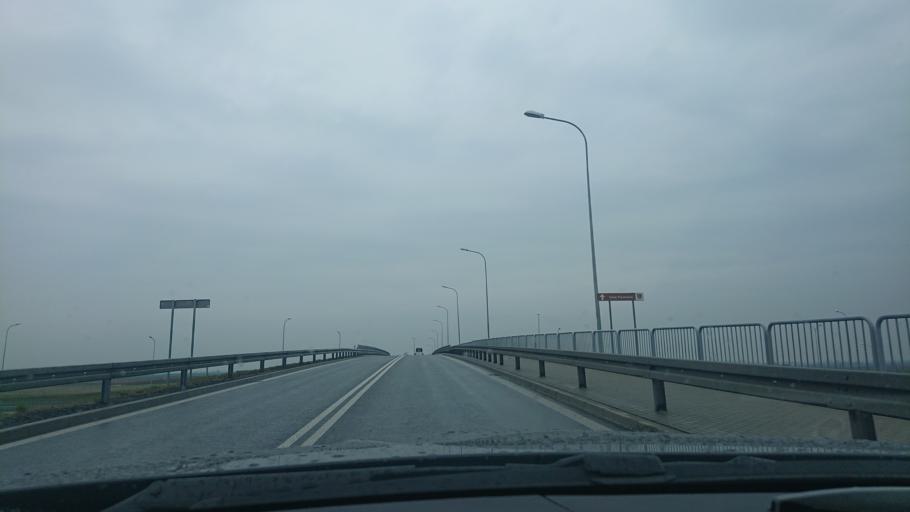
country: PL
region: Greater Poland Voivodeship
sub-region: Powiat gnieznienski
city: Gniezno
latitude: 52.5543
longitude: 17.5430
